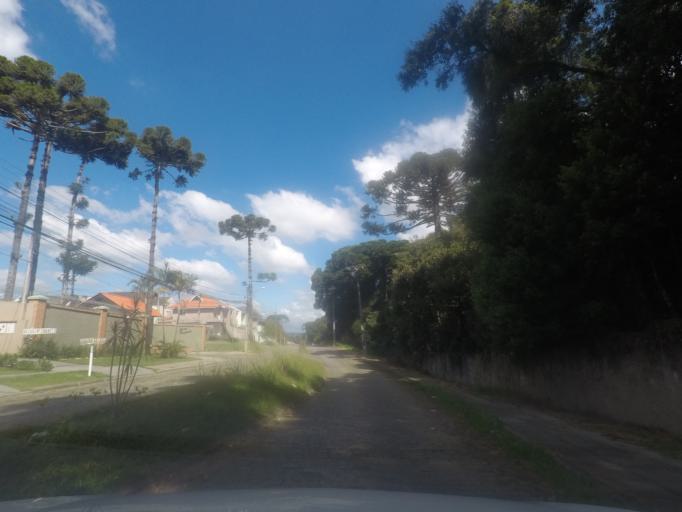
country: BR
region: Parana
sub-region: Pinhais
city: Pinhais
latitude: -25.4748
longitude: -49.2207
